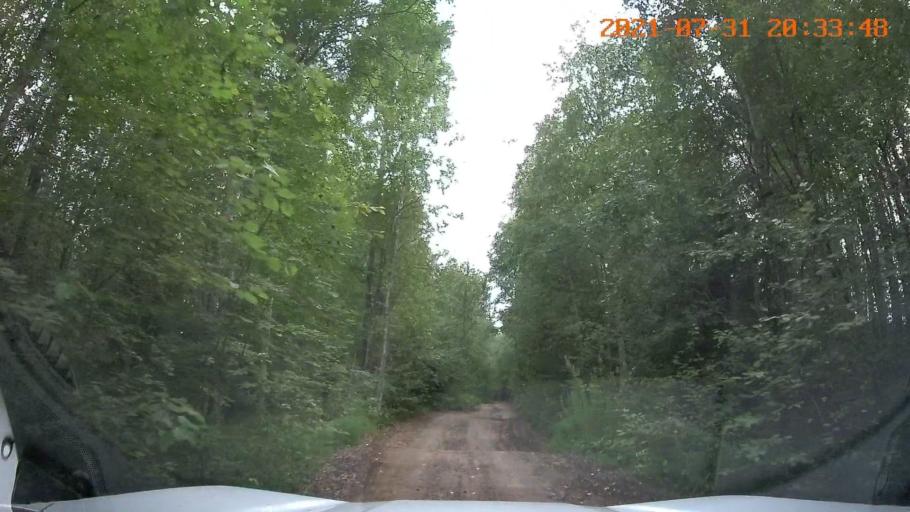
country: RU
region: Republic of Karelia
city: Shal'skiy
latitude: 61.6613
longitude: 36.2676
